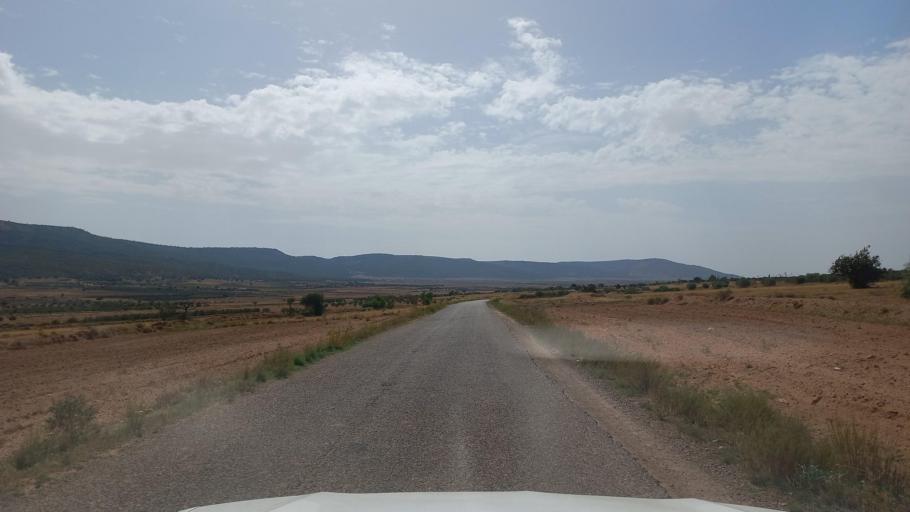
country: TN
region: Al Qasrayn
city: Kasserine
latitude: 35.3687
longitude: 8.8846
